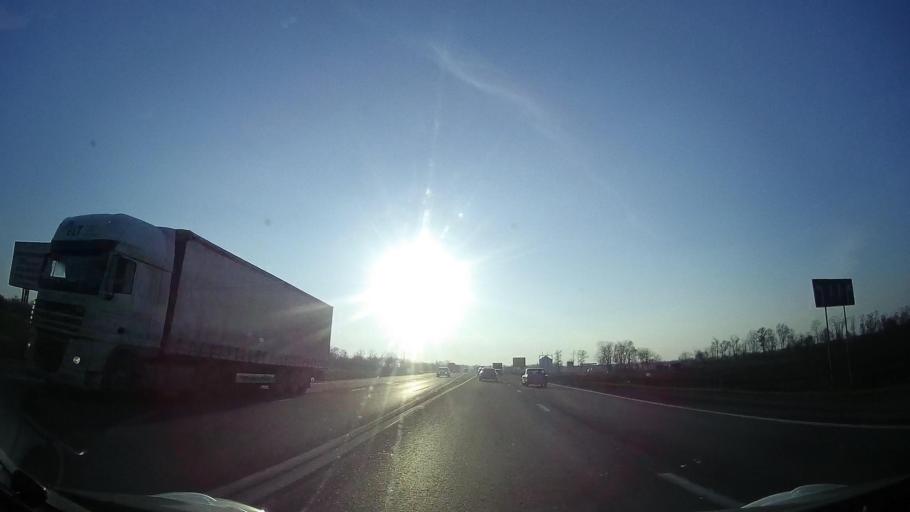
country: RU
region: Rostov
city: Bataysk
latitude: 47.0854
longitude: 39.7830
